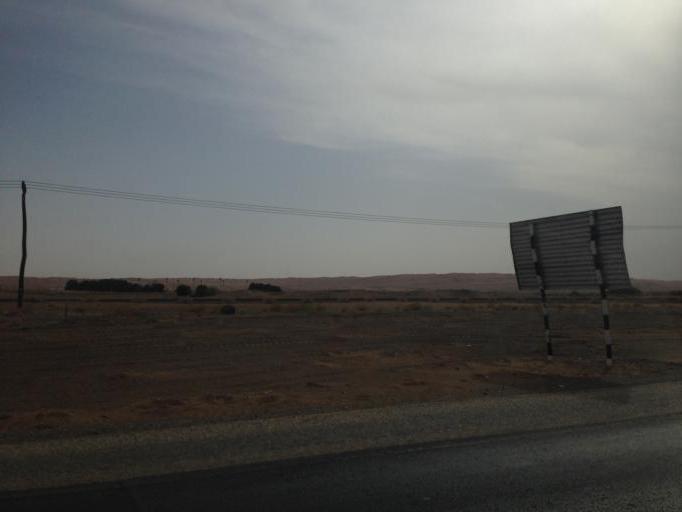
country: OM
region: Ash Sharqiyah
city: Badiyah
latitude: 22.5072
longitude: 58.7442
